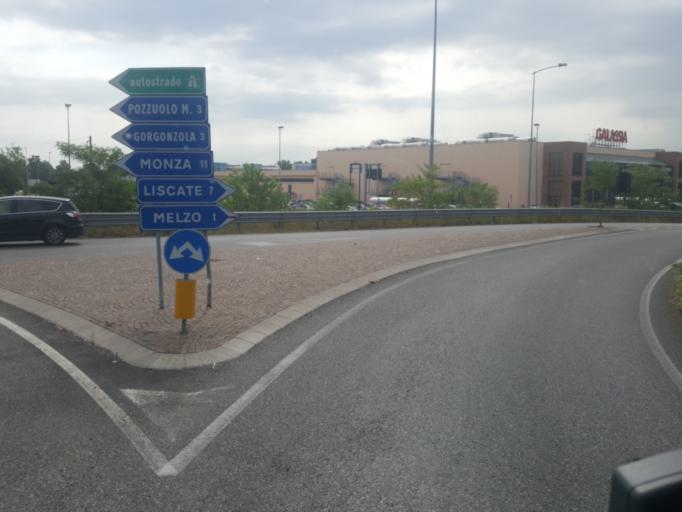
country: IT
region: Lombardy
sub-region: Citta metropolitana di Milano
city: Melzo
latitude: 45.5092
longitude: 9.4099
